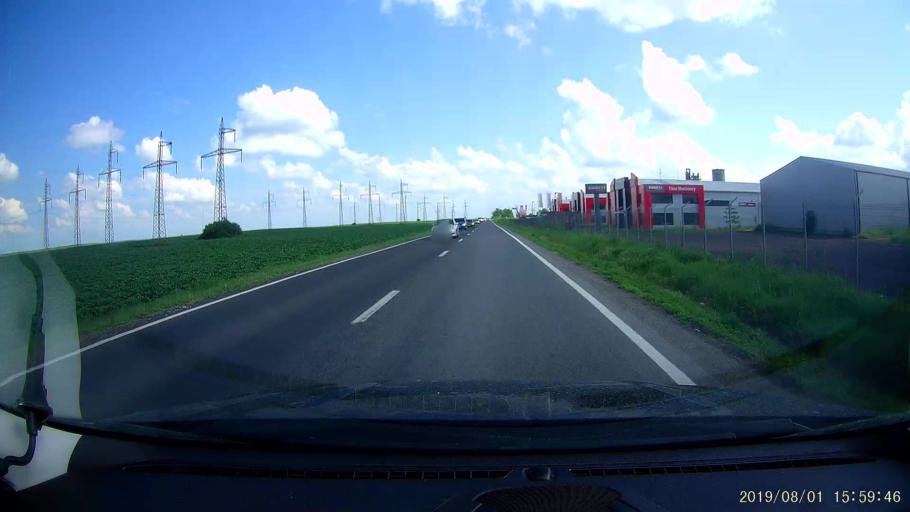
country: RO
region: Ialomita
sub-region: Comuna Slobozia
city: Slobozia
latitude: 44.5410
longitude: 27.3858
